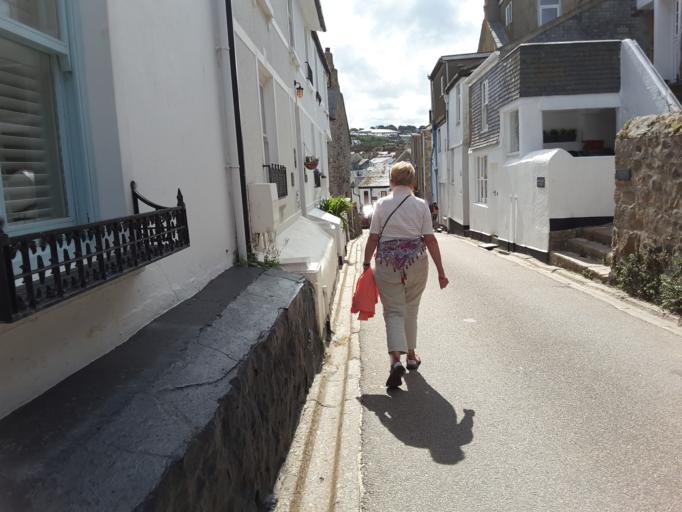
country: GB
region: England
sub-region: Cornwall
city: St Ives
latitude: 50.2158
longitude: -5.4786
